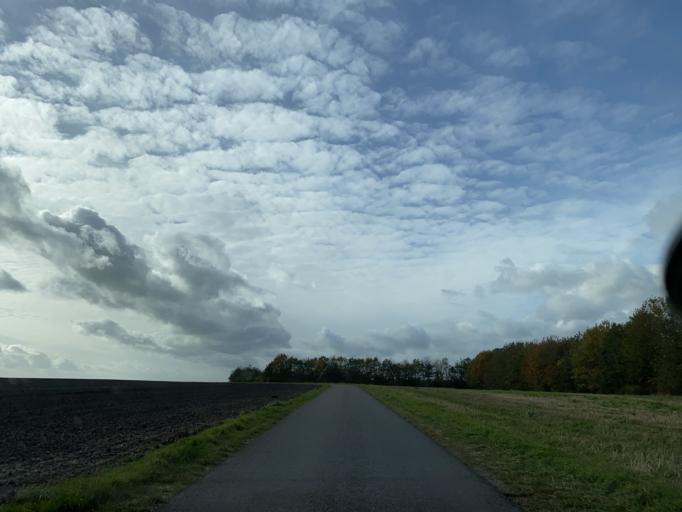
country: DK
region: Central Jutland
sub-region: Arhus Kommune
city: Sabro
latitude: 56.2086
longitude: 9.9981
